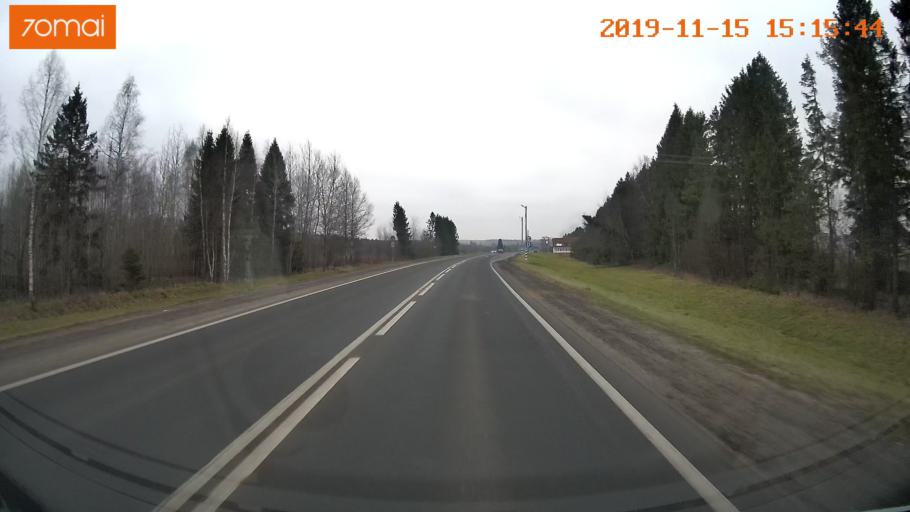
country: RU
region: Jaroslavl
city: Danilov
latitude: 58.2806
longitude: 40.1975
